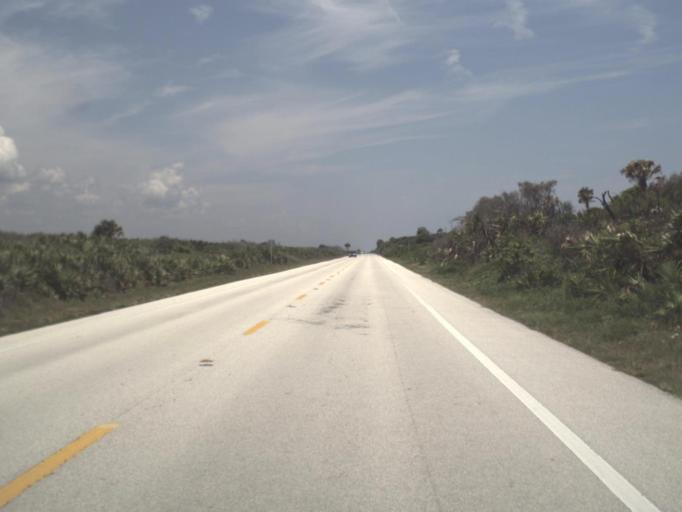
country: US
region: Florida
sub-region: Saint Johns County
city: Palm Valley
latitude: 30.0956
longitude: -81.3404
